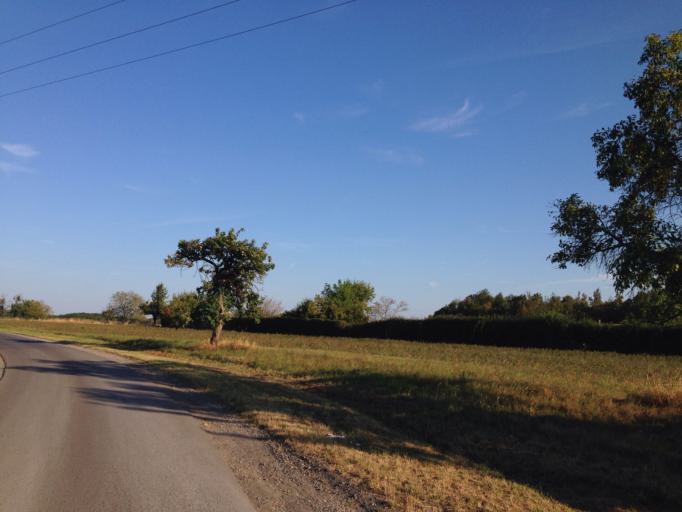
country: DE
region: Hesse
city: Lollar
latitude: 50.6267
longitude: 8.6965
